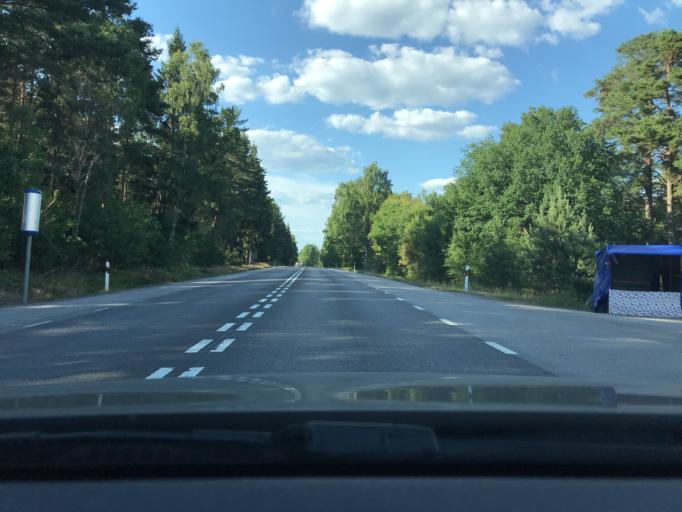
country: SE
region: Kronoberg
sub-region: Vaxjo Kommun
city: Vaexjoe
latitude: 56.8566
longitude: 14.7310
